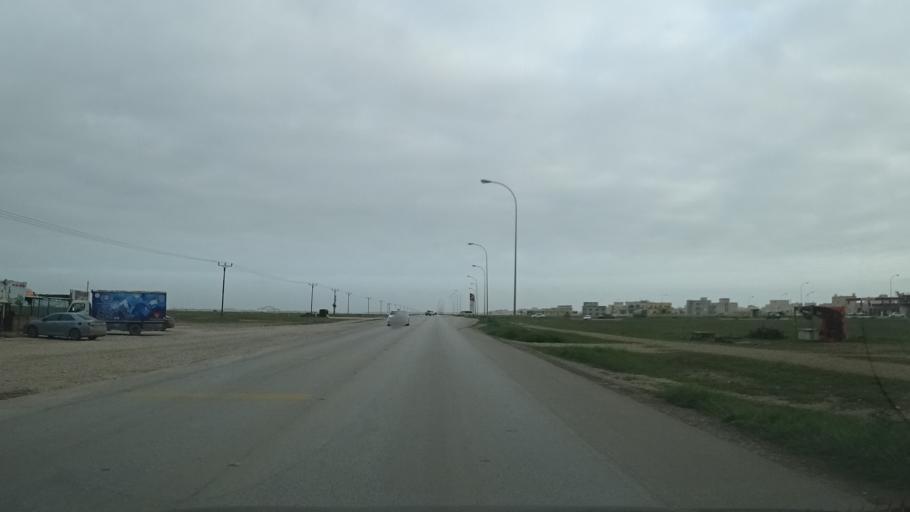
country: OM
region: Zufar
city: Salalah
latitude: 17.0994
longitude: 54.2167
